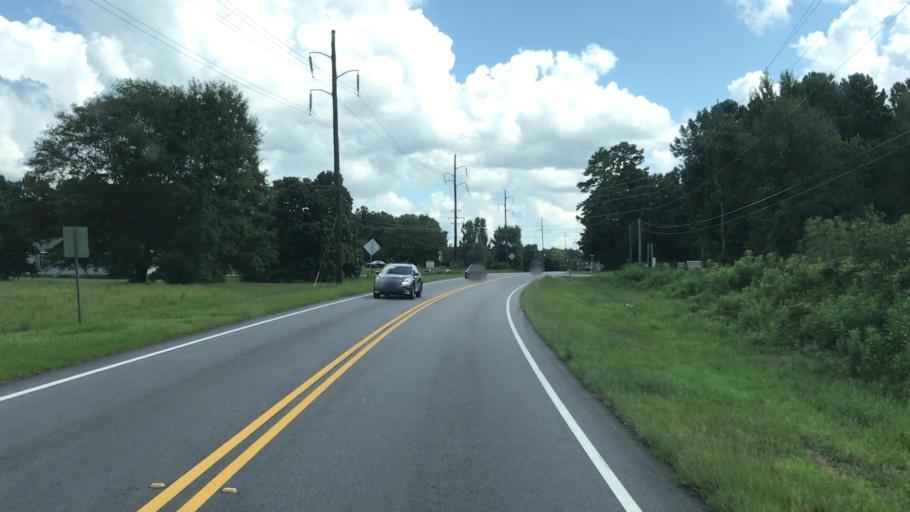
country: US
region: Georgia
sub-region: Newton County
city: Oxford
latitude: 33.6458
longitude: -83.8353
